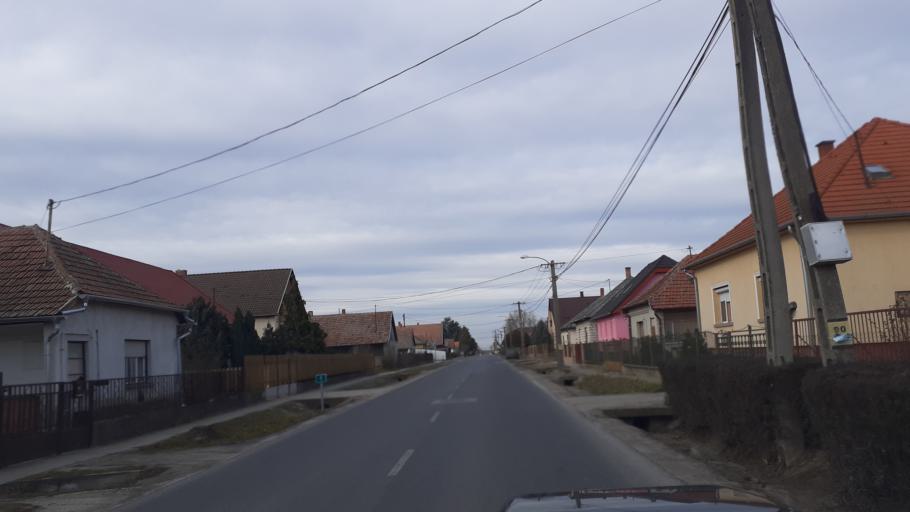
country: HU
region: Fejer
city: Sarbogard
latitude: 46.8993
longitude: 18.6041
